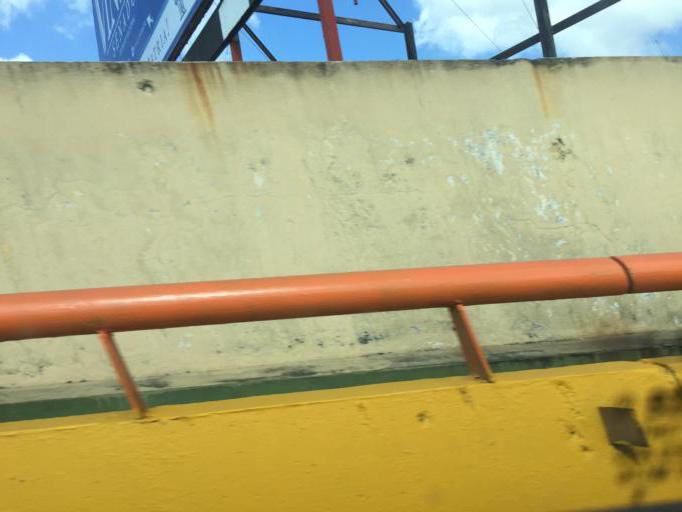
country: DO
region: Nacional
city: San Carlos
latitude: 18.4842
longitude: -69.8909
